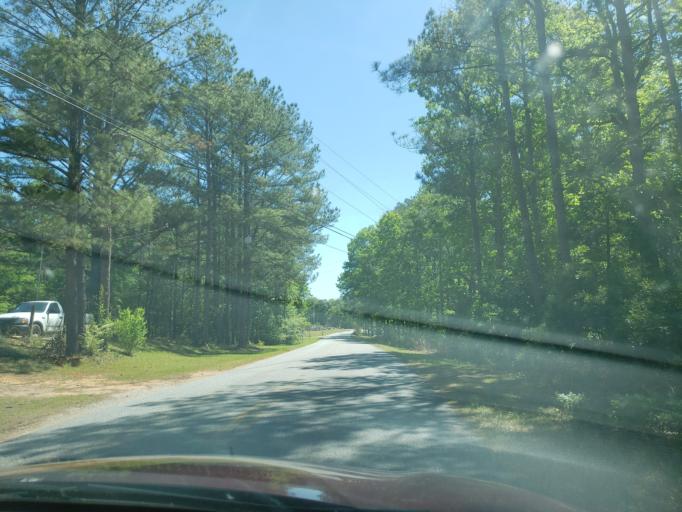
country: US
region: Alabama
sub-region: Tallapoosa County
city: Dadeville
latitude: 32.6973
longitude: -85.8546
